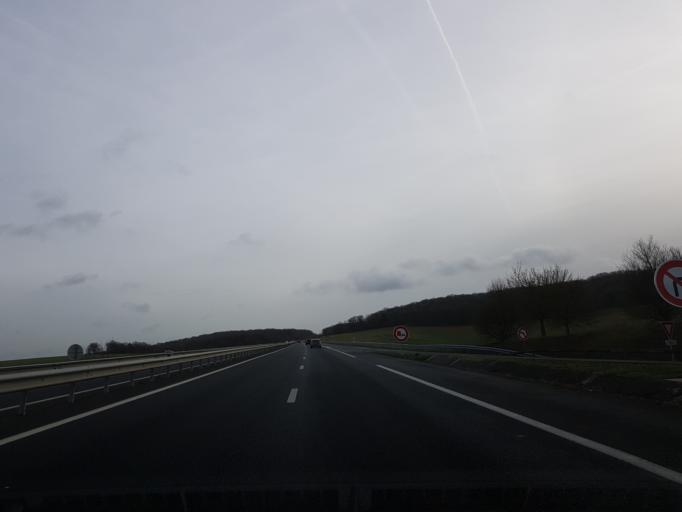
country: FR
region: Bourgogne
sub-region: Departement de l'Yonne
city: Soucy
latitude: 48.2462
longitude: 3.3506
